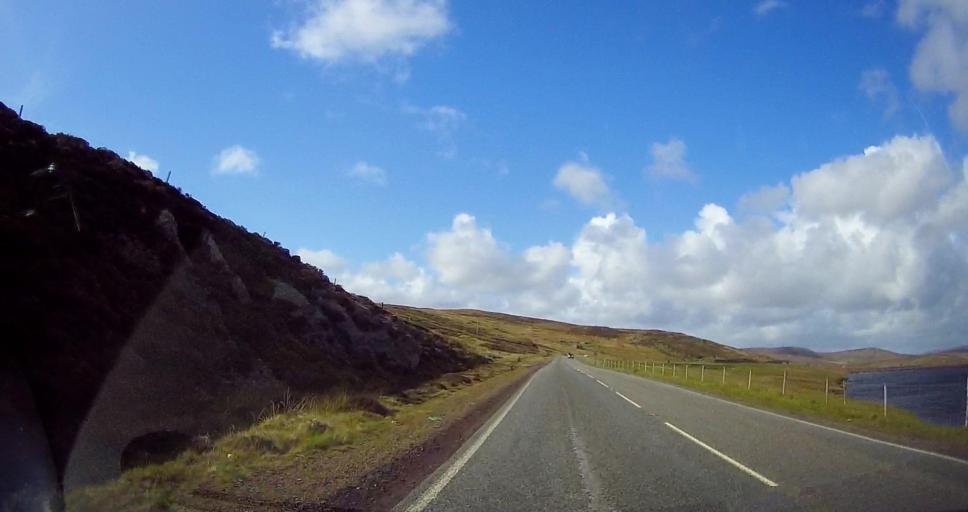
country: GB
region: Scotland
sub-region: Shetland Islands
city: Lerwick
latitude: 60.2512
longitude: -1.2255
